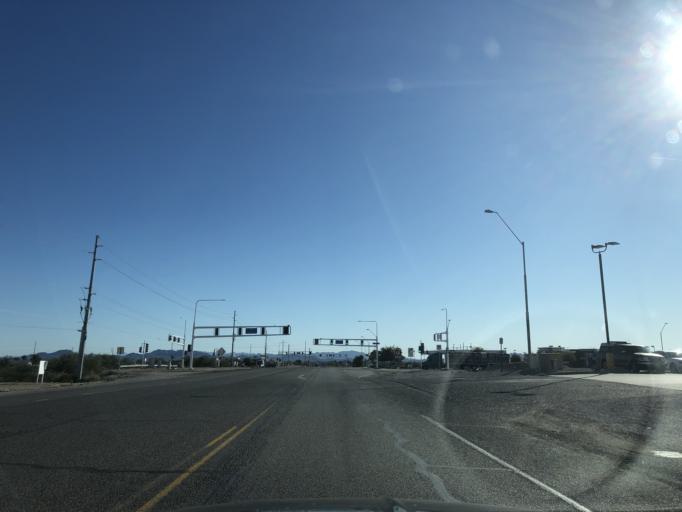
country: US
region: Arizona
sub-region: Maricopa County
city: Buckeye
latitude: 33.4314
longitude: -112.5909
